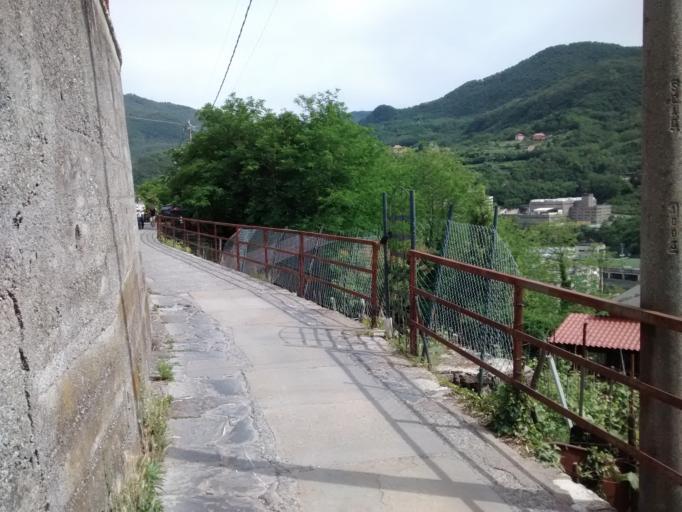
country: IT
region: Liguria
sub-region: Provincia di Genova
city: Piccarello
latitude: 44.4516
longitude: 8.9984
